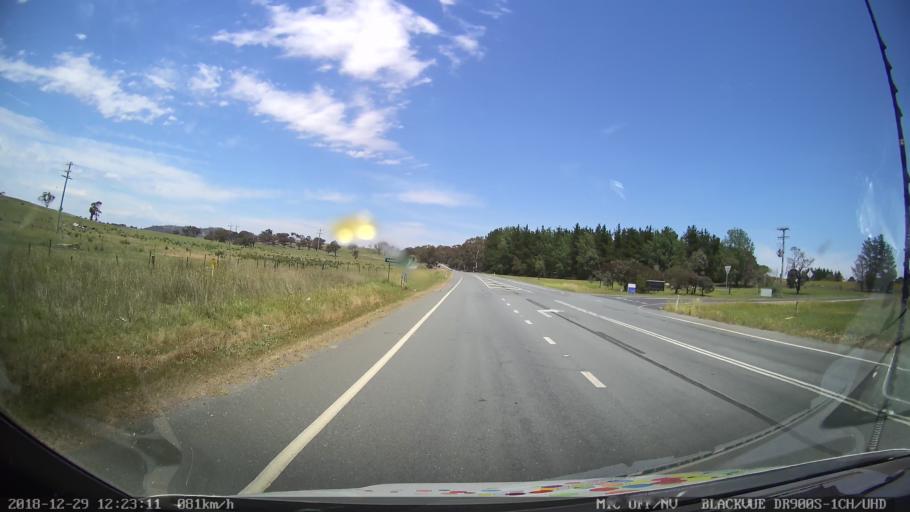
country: AU
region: New South Wales
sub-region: Queanbeyan
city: Queanbeyan
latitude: -35.4333
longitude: 149.2172
